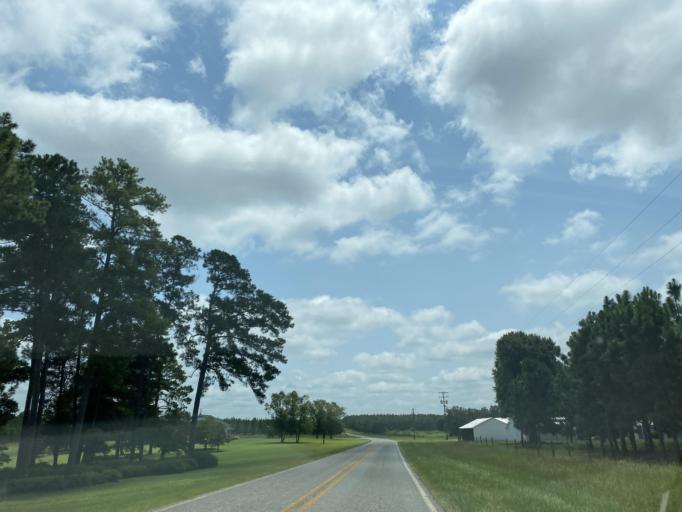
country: US
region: Georgia
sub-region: Wheeler County
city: Alamo
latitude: 32.0698
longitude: -82.7307
